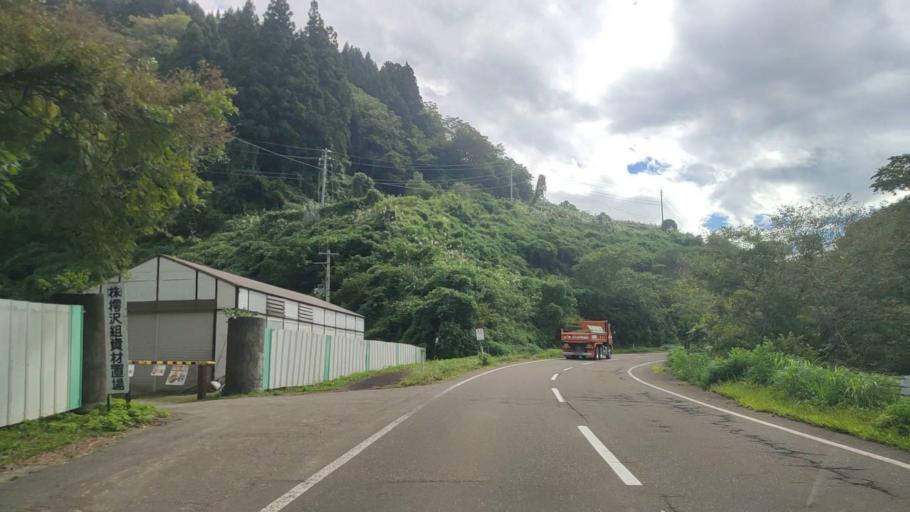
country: JP
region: Niigata
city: Arai
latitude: 36.9358
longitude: 138.2948
